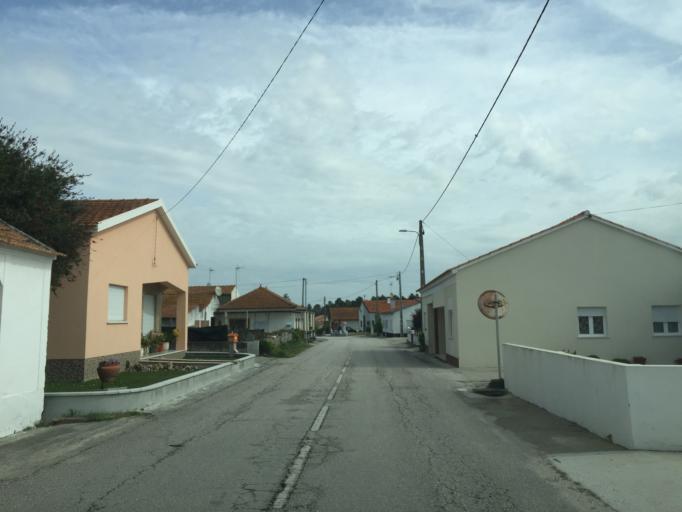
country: PT
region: Coimbra
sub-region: Figueira da Foz
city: Lavos
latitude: 40.0158
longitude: -8.8233
